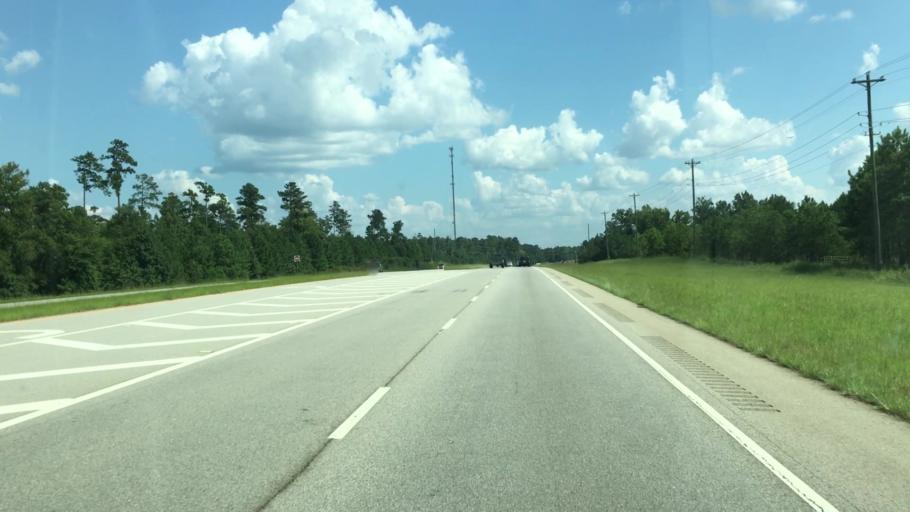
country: US
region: Georgia
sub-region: Putnam County
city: Eatonton
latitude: 33.2137
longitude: -83.3027
